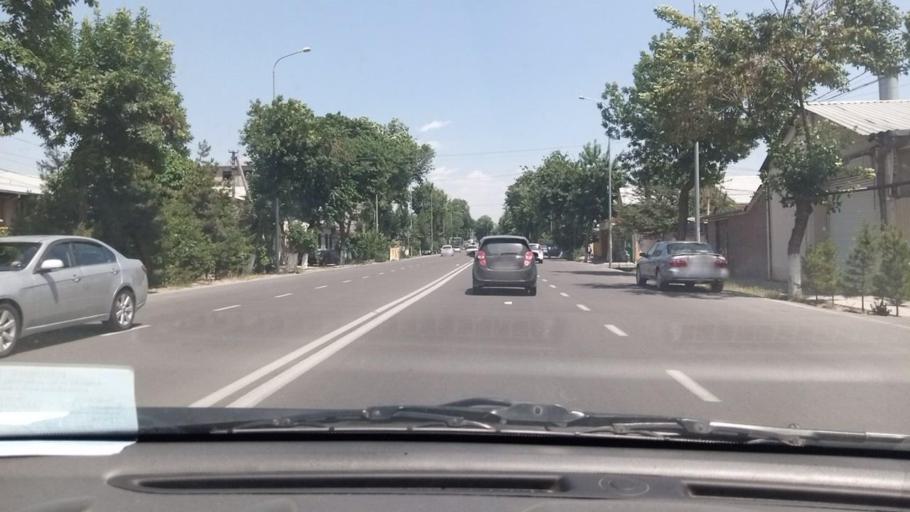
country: UZ
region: Toshkent Shahri
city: Tashkent
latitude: 41.2826
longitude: 69.2793
